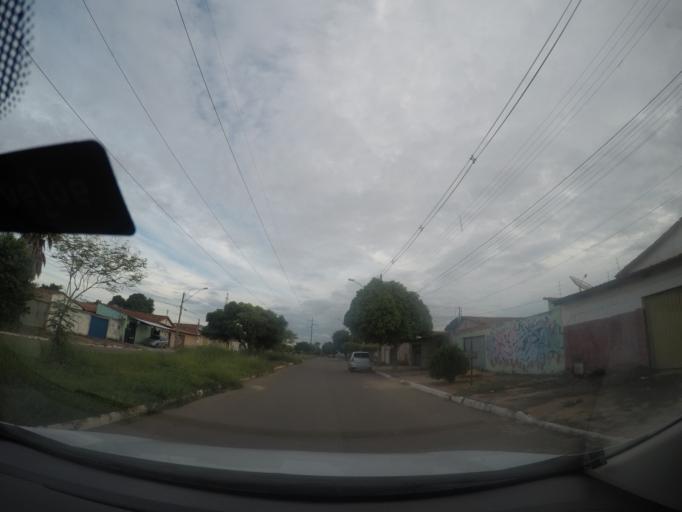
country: BR
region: Goias
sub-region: Goianira
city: Goianira
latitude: -16.5866
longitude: -49.3772
